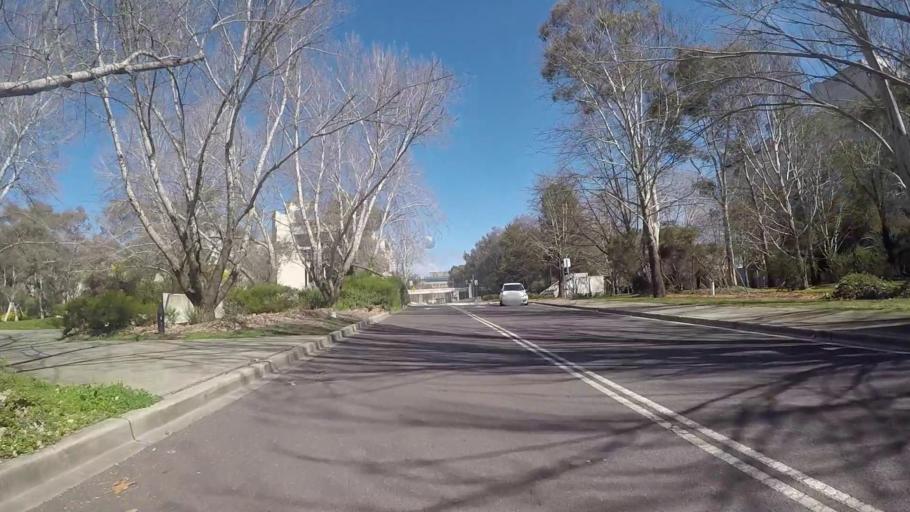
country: AU
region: Australian Capital Territory
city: Canberra
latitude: -35.2990
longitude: 149.1372
